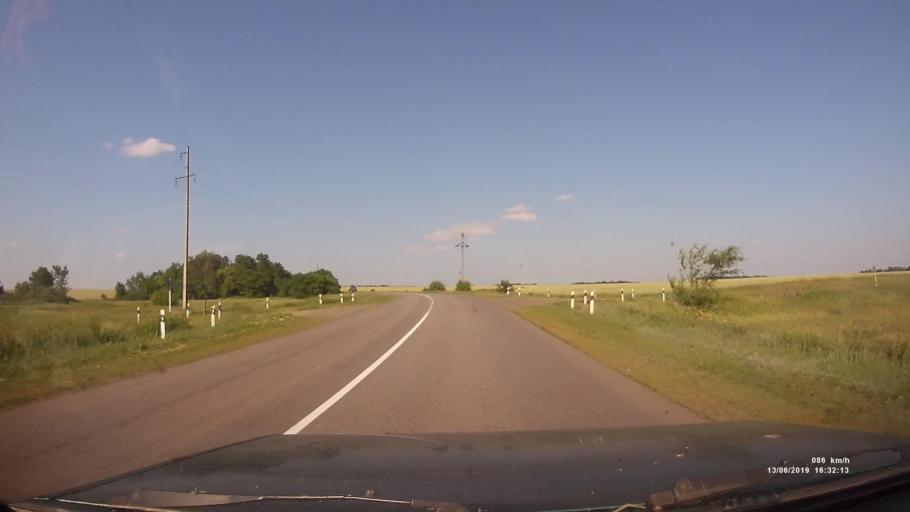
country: RU
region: Rostov
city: Kazanskaya
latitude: 49.8461
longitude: 41.2686
